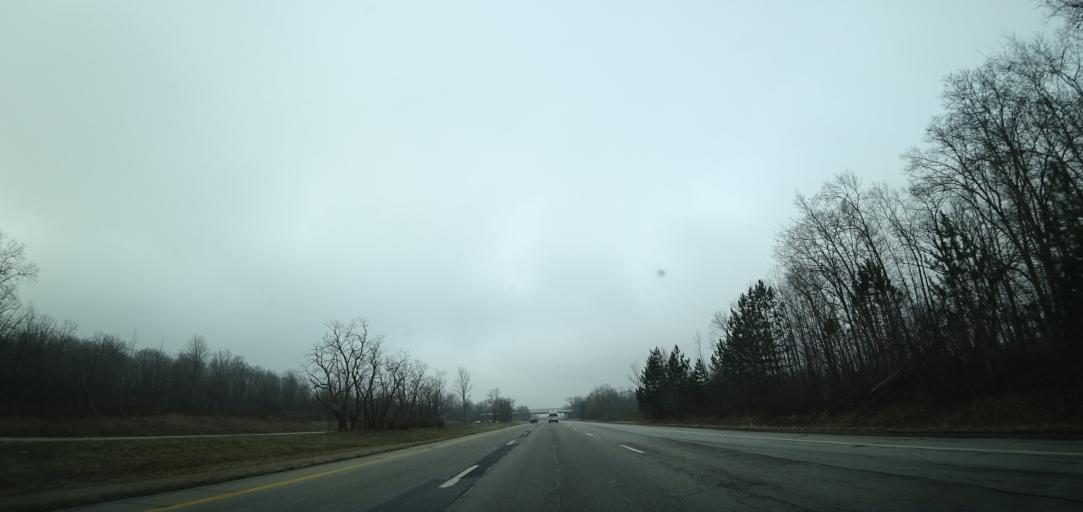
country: US
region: Ohio
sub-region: Summit County
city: Richfield
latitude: 41.2153
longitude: -81.6263
